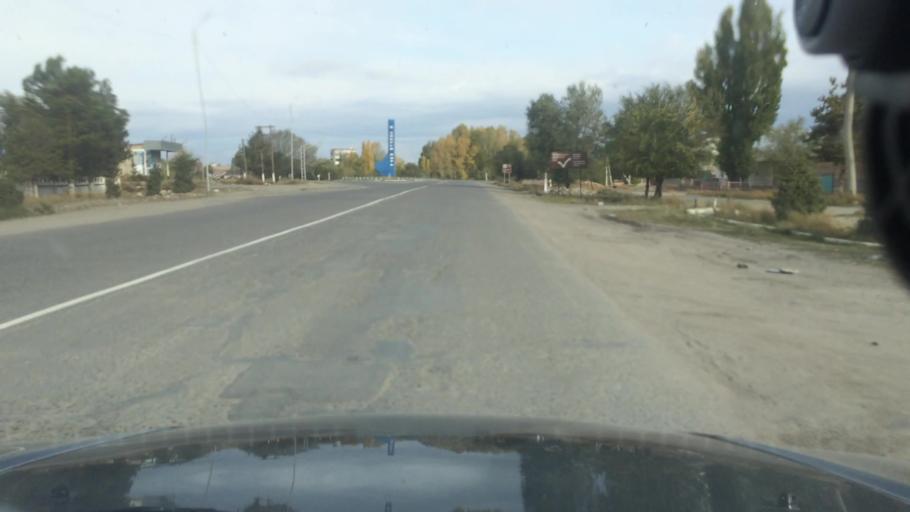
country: KG
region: Ysyk-Koel
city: Karakol
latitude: 42.5312
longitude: 78.3826
